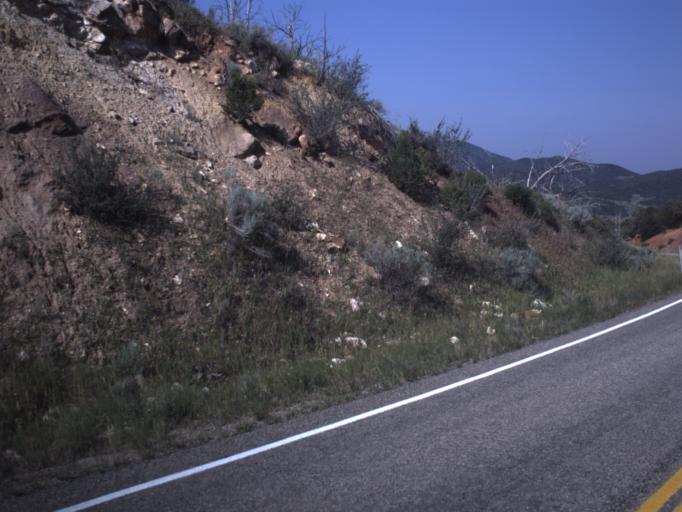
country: US
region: Utah
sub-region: Daggett County
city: Manila
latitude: 40.9533
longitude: -109.4516
